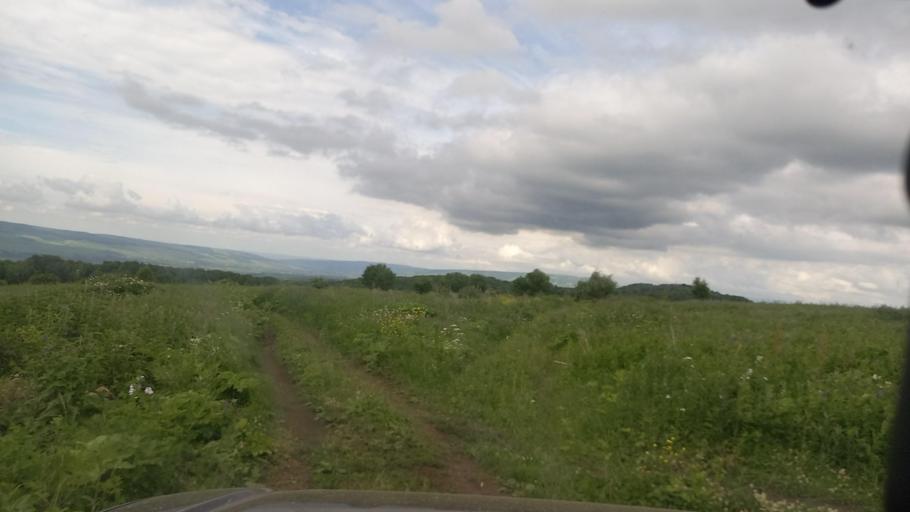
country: RU
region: Krasnodarskiy
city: Peredovaya
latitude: 44.0440
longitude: 41.3352
